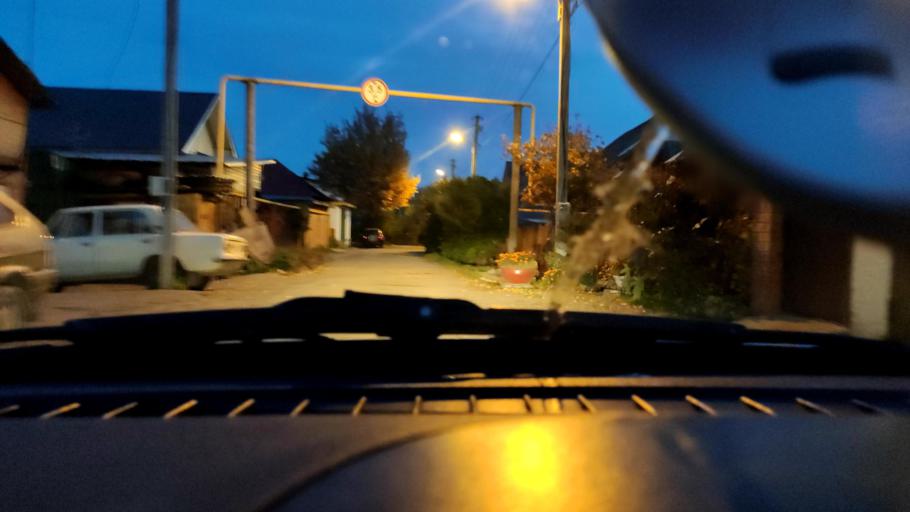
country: RU
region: Perm
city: Kondratovo
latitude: 57.9980
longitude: 56.1207
